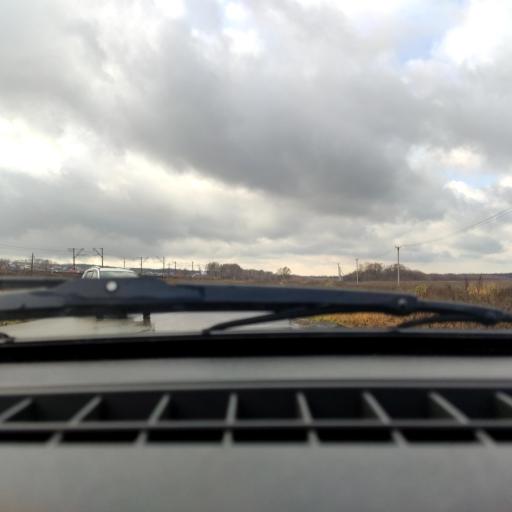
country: RU
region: Bashkortostan
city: Kabakovo
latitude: 54.6410
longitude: 56.0781
